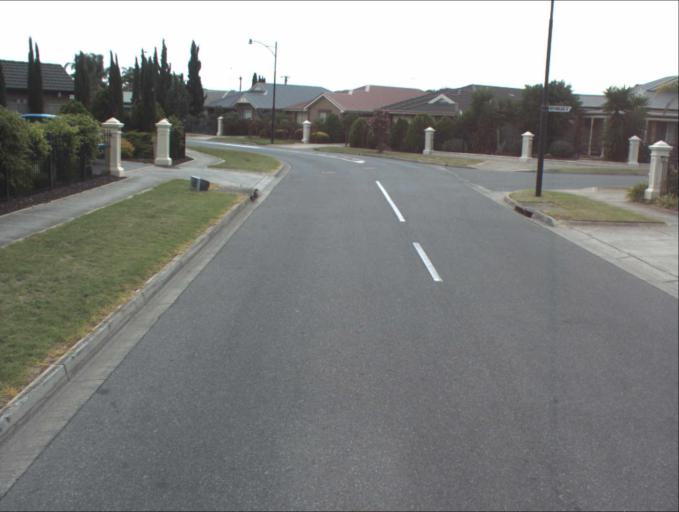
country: AU
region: South Australia
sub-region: Charles Sturt
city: Woodville
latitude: -34.8728
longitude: 138.5620
